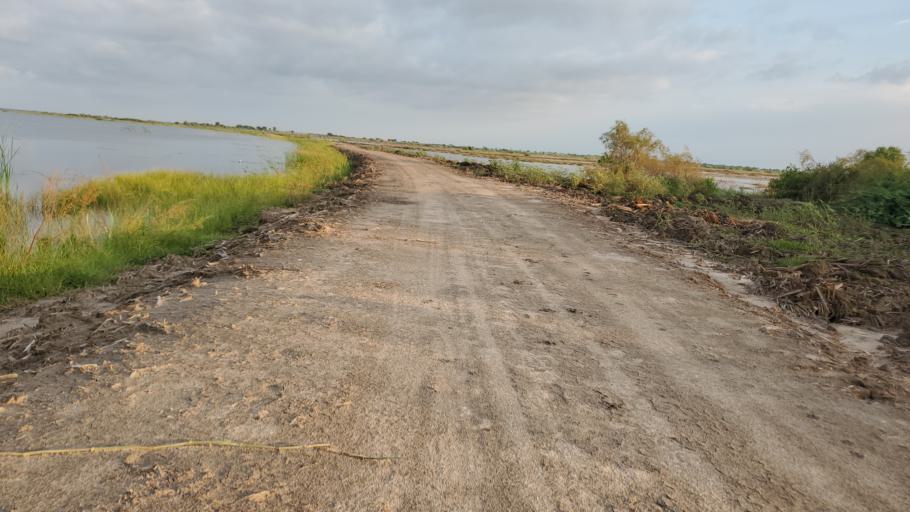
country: SN
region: Saint-Louis
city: Saint-Louis
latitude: 16.0239
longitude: -16.4096
